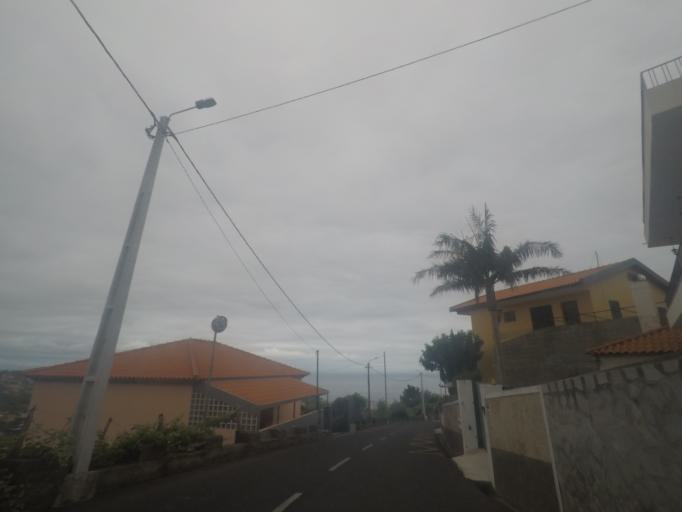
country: PT
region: Madeira
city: Camara de Lobos
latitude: 32.6642
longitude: -16.9636
